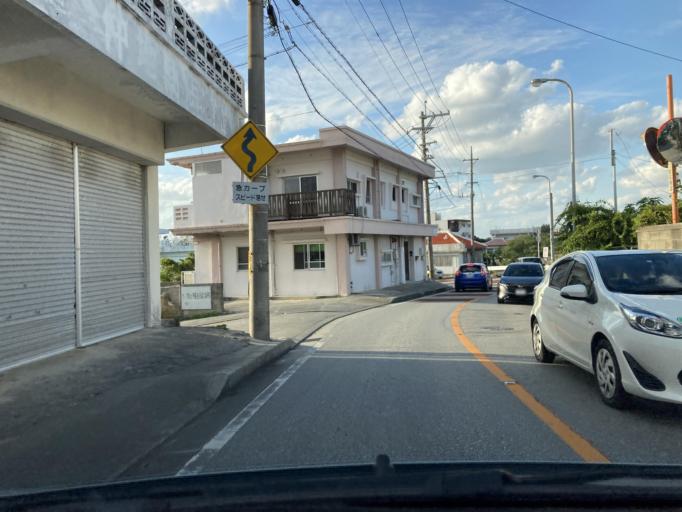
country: JP
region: Okinawa
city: Chatan
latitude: 26.3141
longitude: 127.7700
